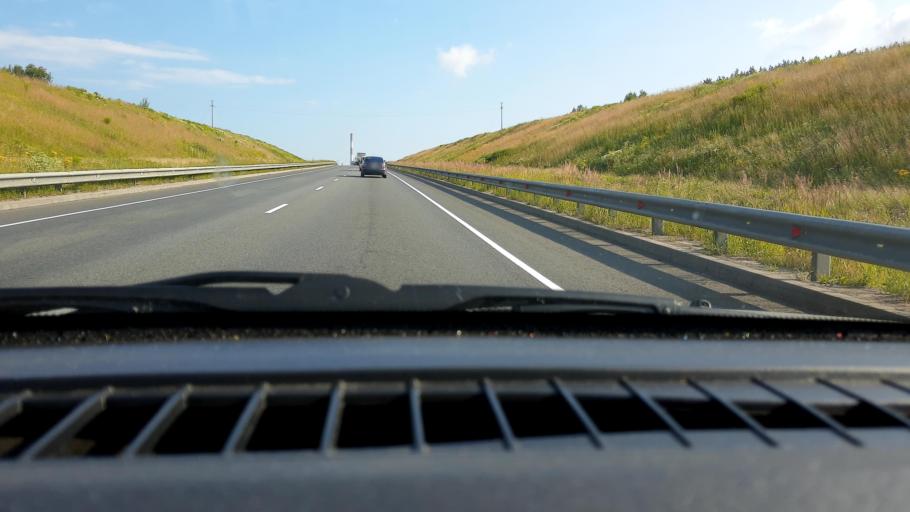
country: RU
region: Nizjnij Novgorod
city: Kstovo
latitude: 56.0821
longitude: 44.1351
